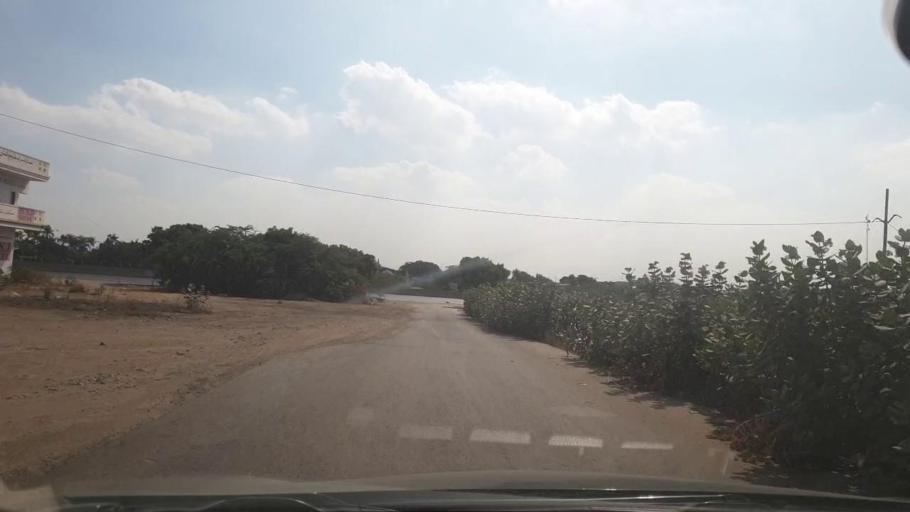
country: PK
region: Sindh
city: Malir Cantonment
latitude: 25.0079
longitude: 67.3562
